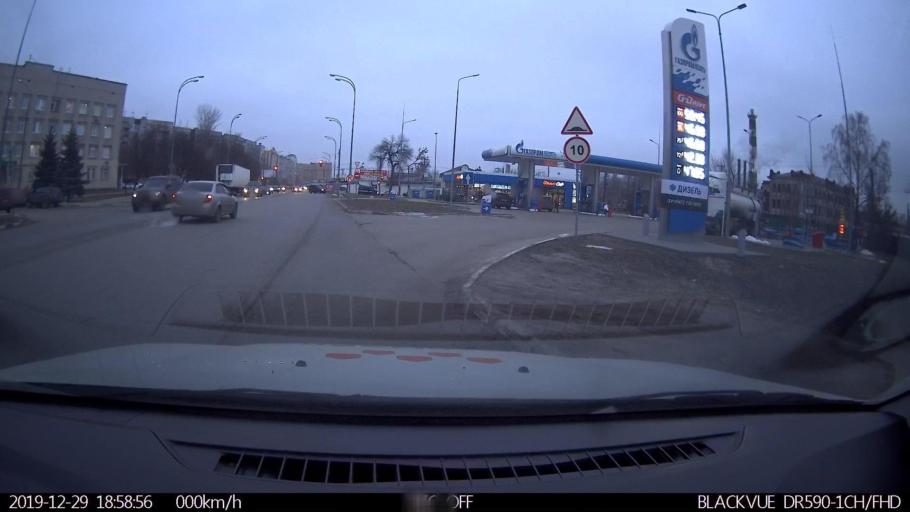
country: RU
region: Nizjnij Novgorod
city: Neklyudovo
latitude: 56.3503
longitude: 43.8757
